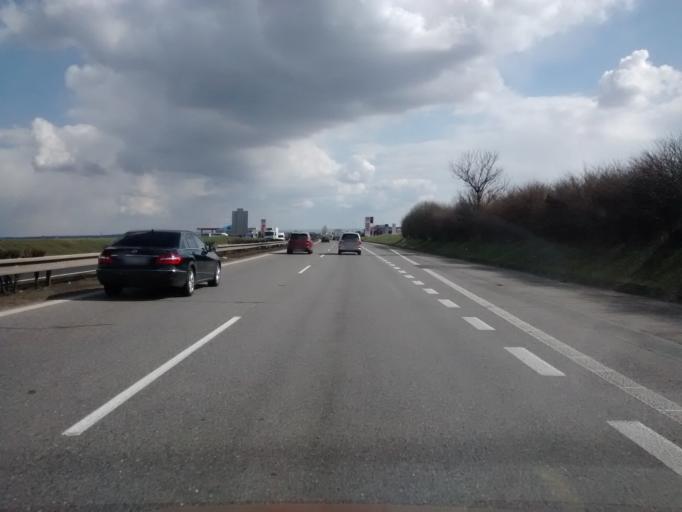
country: CZ
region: Central Bohemia
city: Zdiby
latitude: 50.1722
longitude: 14.4572
